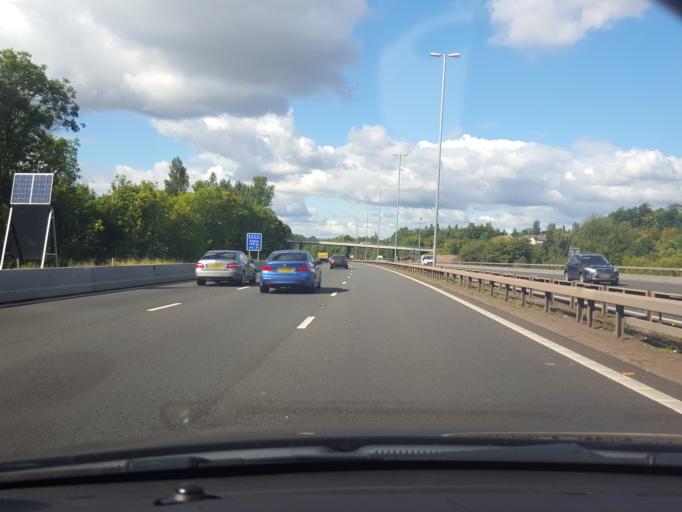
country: GB
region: Scotland
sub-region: South Lanarkshire
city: Uddingston
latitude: 55.8247
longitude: -4.0773
